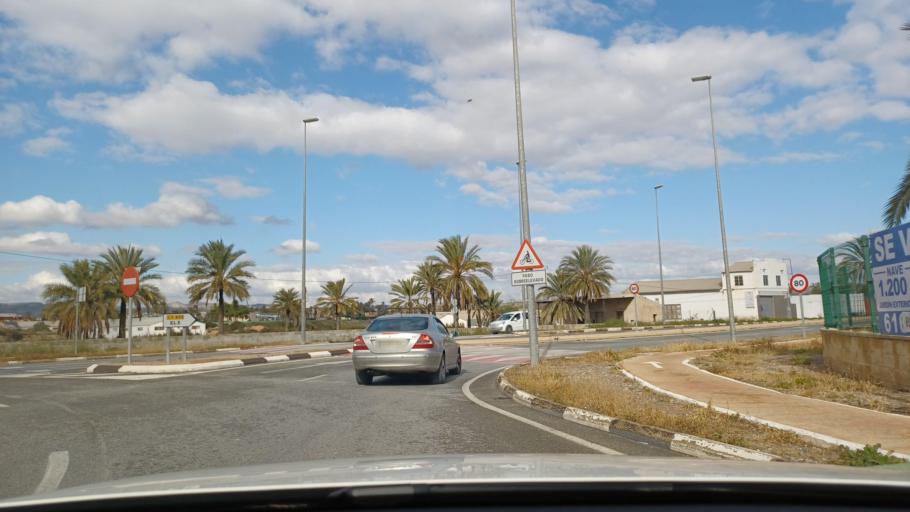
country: ES
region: Valencia
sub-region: Provincia de Alicante
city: Elche
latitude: 38.2433
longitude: -0.6996
